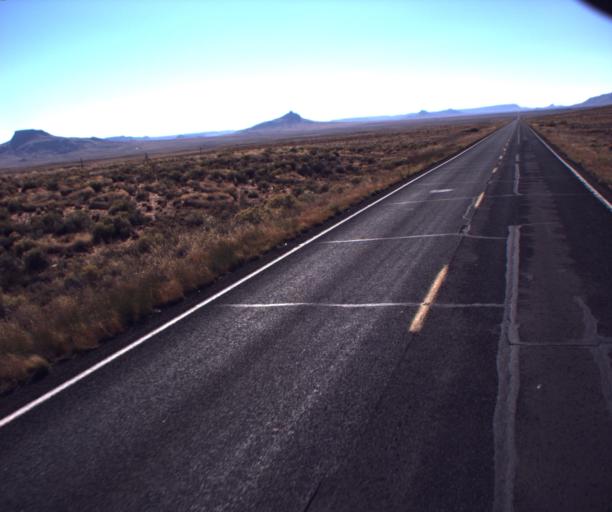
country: US
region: Arizona
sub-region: Navajo County
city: First Mesa
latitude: 35.6082
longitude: -110.4738
